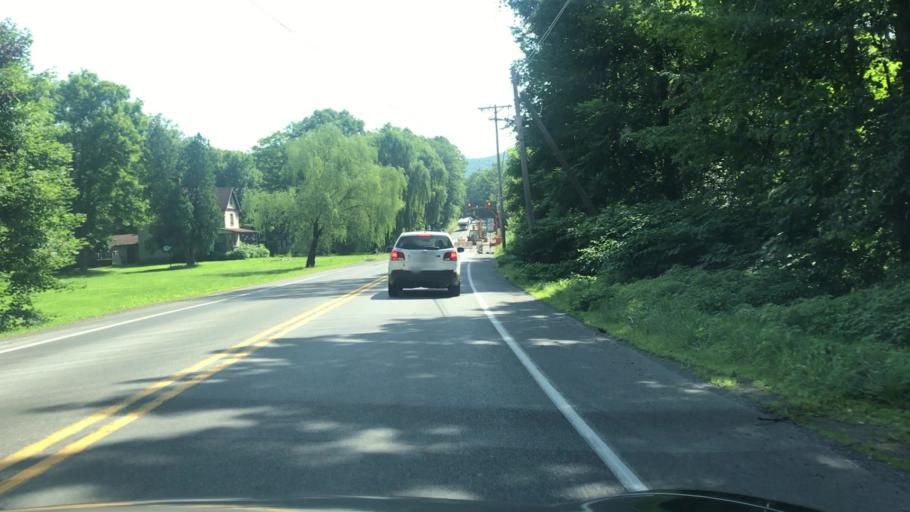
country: US
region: Pennsylvania
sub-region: Lycoming County
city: Garden View
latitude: 41.4221
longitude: -77.0273
